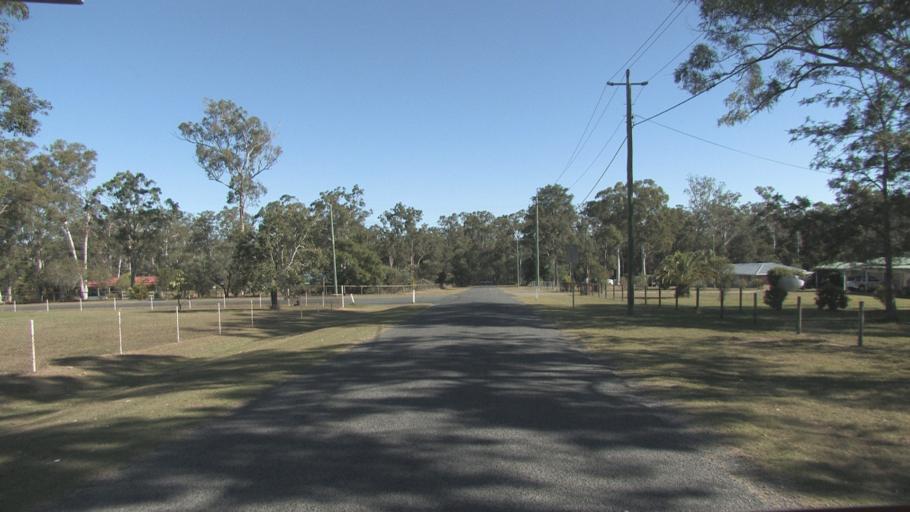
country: AU
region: Queensland
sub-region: Logan
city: Chambers Flat
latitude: -27.7405
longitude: 153.0693
